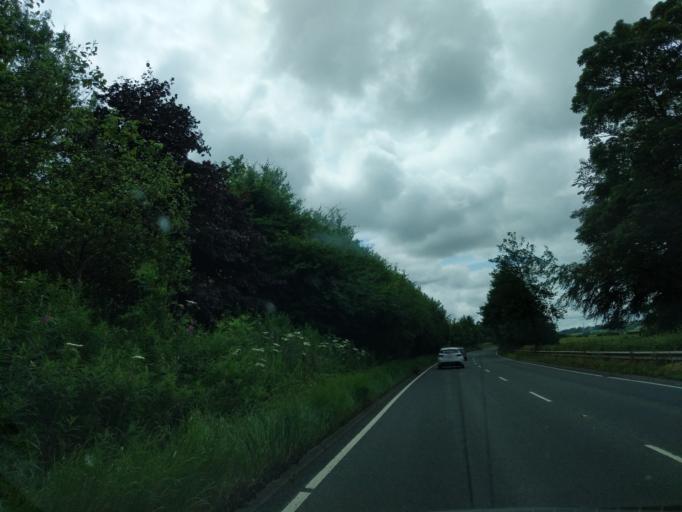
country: GB
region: Scotland
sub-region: South Lanarkshire
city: Larkhall
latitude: 55.7026
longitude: -3.9736
